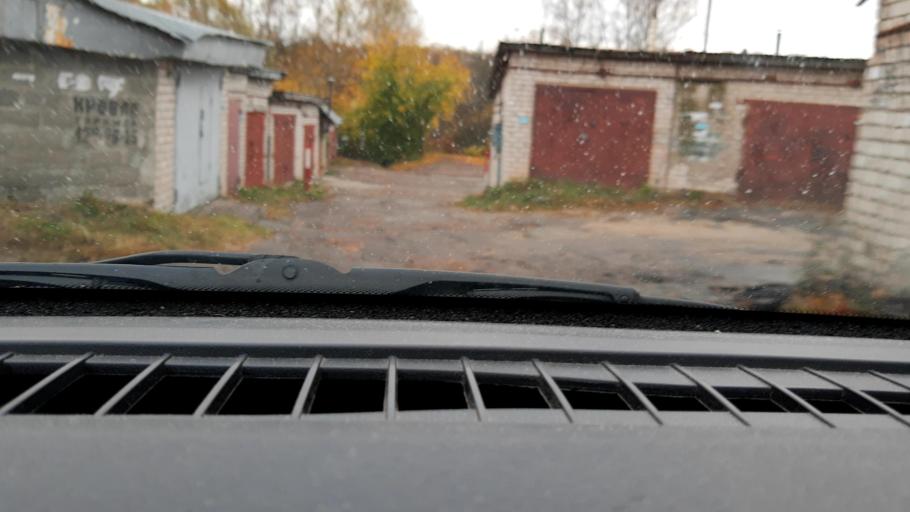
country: RU
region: Nizjnij Novgorod
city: Nizhniy Novgorod
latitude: 56.2298
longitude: 43.9580
